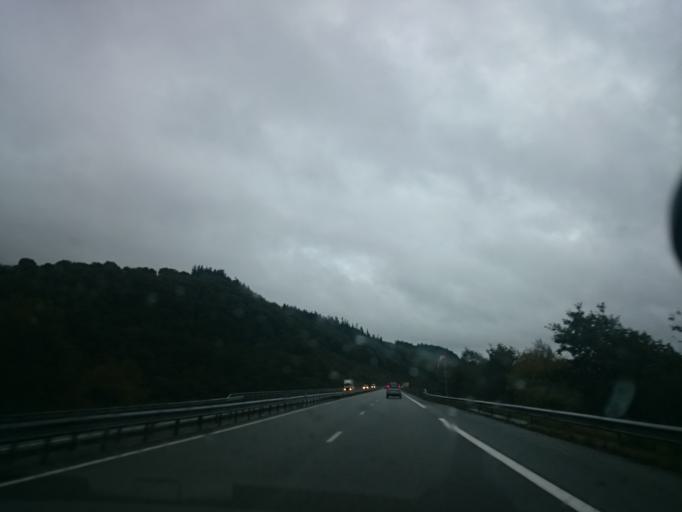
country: FR
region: Brittany
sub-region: Departement du Finistere
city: Chateaulin
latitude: 48.2484
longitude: -4.1108
